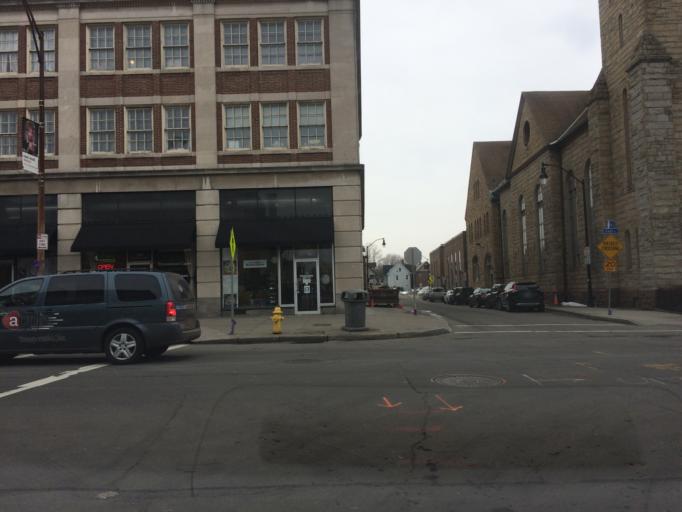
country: US
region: New York
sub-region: Monroe County
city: Rochester
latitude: 43.1555
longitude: -77.5955
